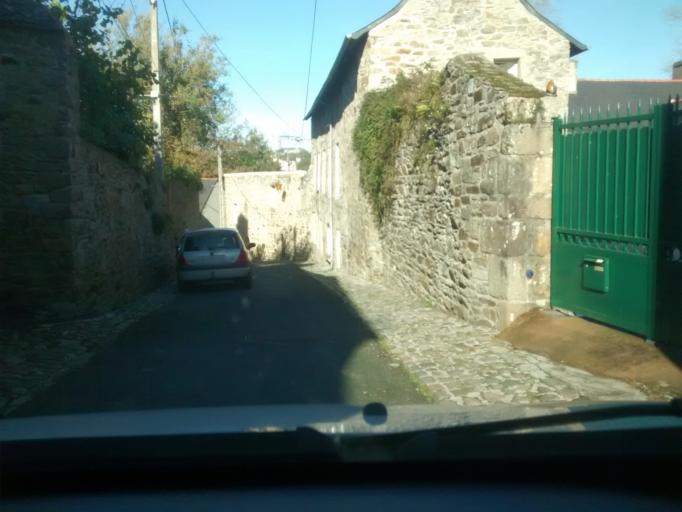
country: FR
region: Brittany
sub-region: Departement des Cotes-d'Armor
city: Treguier
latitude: 48.7879
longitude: -3.2330
